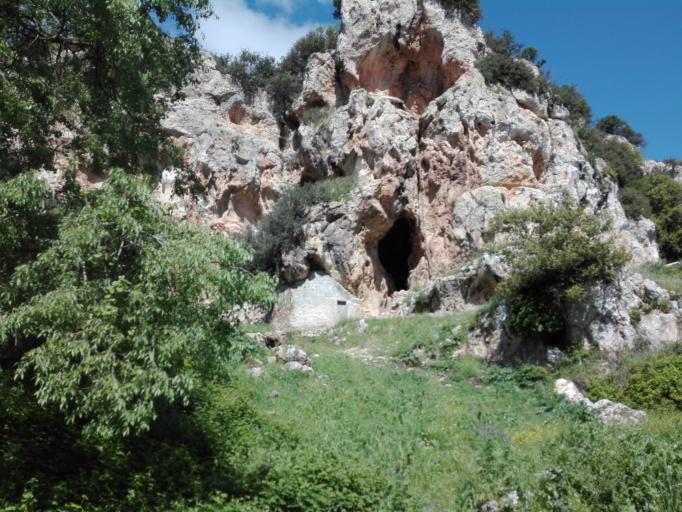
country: IT
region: Sardinia
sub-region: Provincia di Sassari
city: Mara
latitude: 40.4479
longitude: 8.6583
